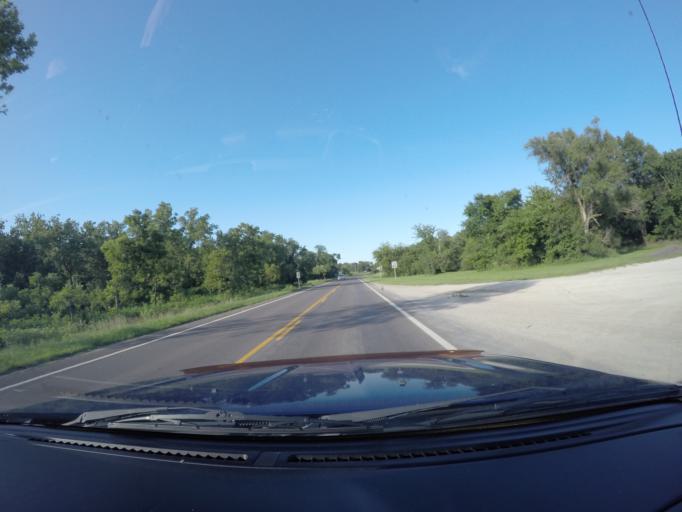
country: US
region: Kansas
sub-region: Douglas County
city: Lawrence
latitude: 39.0051
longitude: -95.1871
